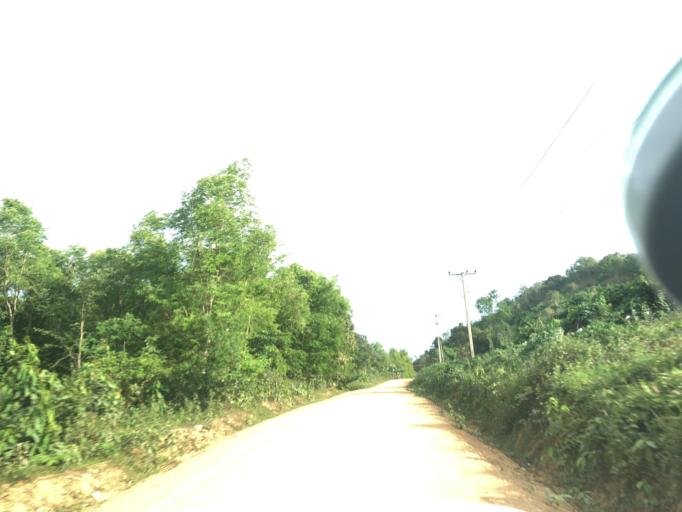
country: TH
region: Loei
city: Chiang Khan
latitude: 18.0235
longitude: 101.4185
